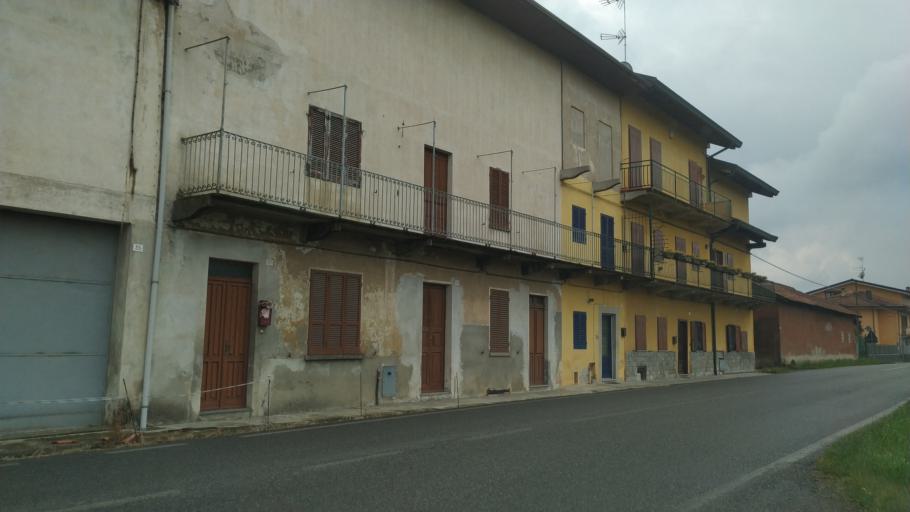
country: IT
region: Piedmont
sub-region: Provincia di Novara
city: Cavallirio
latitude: 45.6616
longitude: 8.3930
